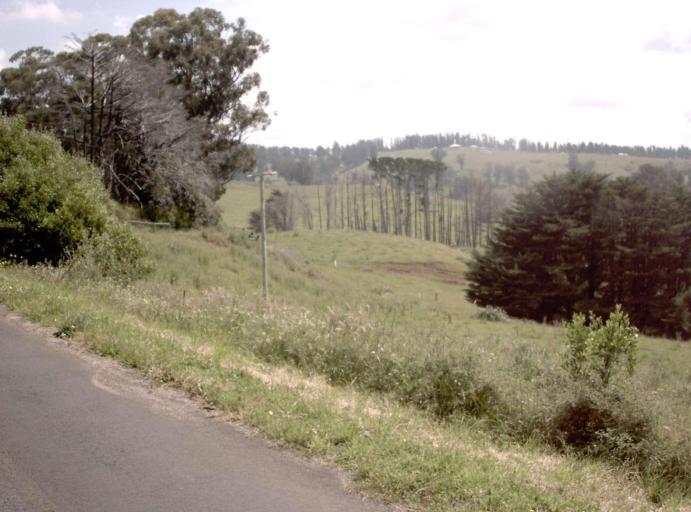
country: AU
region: Victoria
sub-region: Latrobe
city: Traralgon
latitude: -38.3344
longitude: 146.5723
